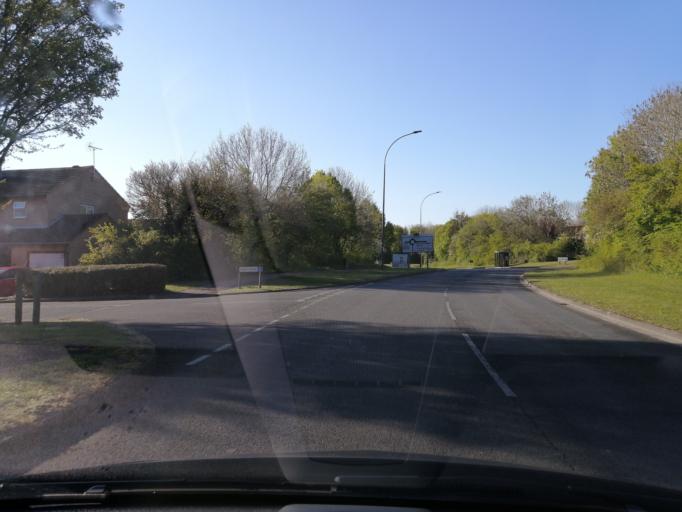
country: GB
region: England
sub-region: Peterborough
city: Castor
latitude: 52.5559
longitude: -0.3061
